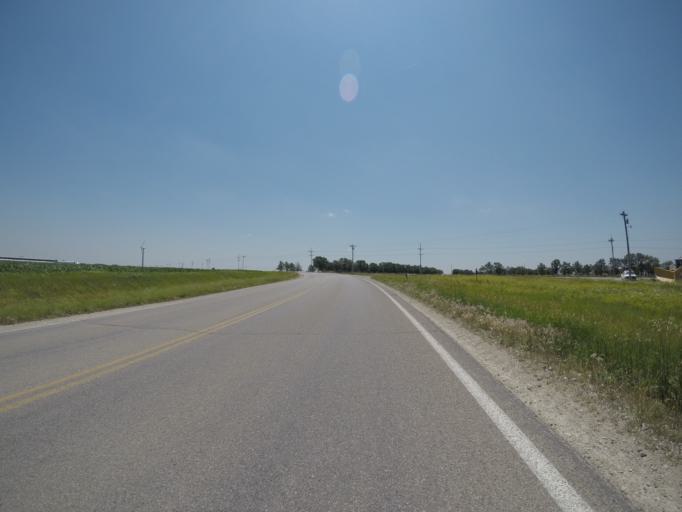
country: US
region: Kansas
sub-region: Riley County
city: Manhattan
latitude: 39.2333
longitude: -96.4447
